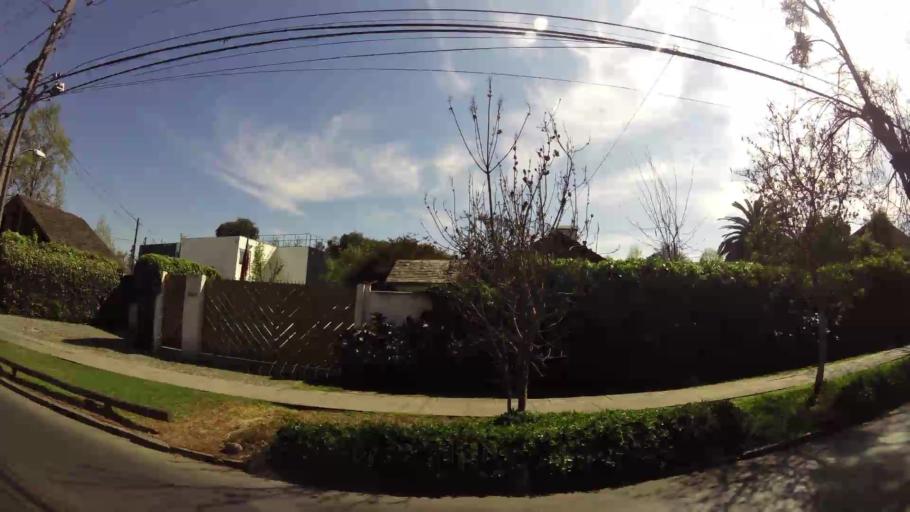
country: CL
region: Santiago Metropolitan
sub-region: Provincia de Santiago
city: Villa Presidente Frei, Nunoa, Santiago, Chile
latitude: -33.4422
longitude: -70.5525
